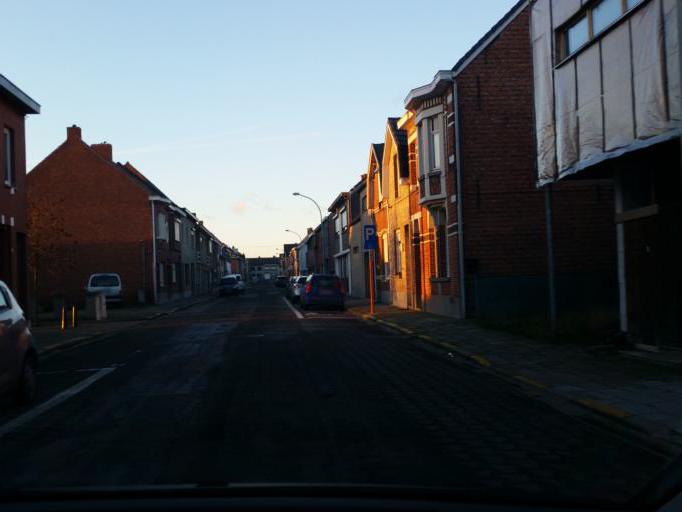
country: BE
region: Flanders
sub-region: Provincie Oost-Vlaanderen
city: Sint-Gillis-Waas
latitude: 51.2903
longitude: 4.1685
